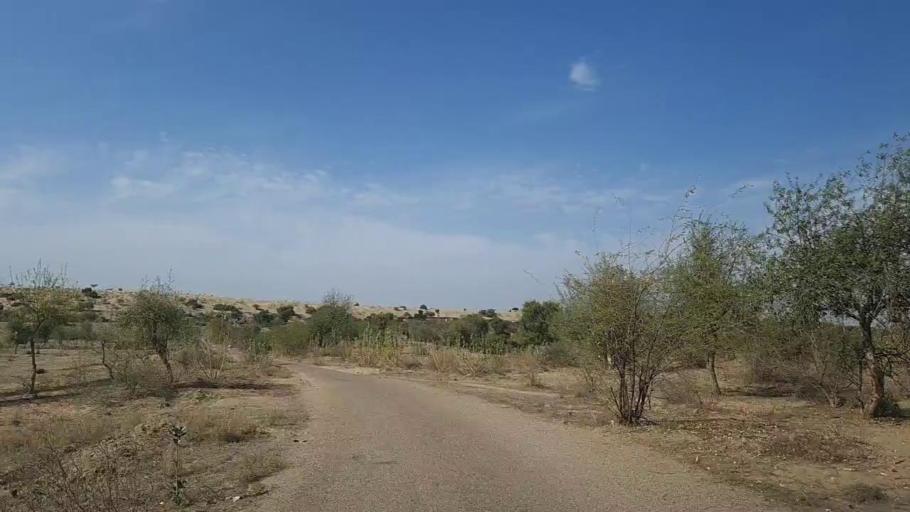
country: PK
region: Sindh
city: Naukot
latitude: 24.8318
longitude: 69.5480
